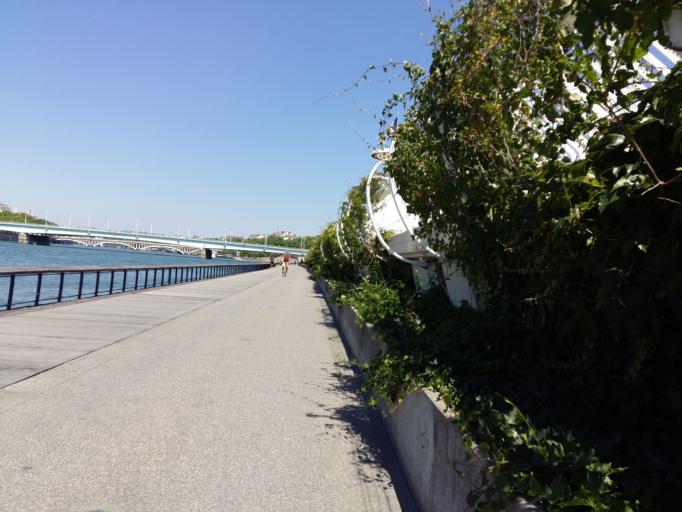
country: FR
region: Rhone-Alpes
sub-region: Departement du Rhone
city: Lyon
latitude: 45.7539
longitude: 4.8377
